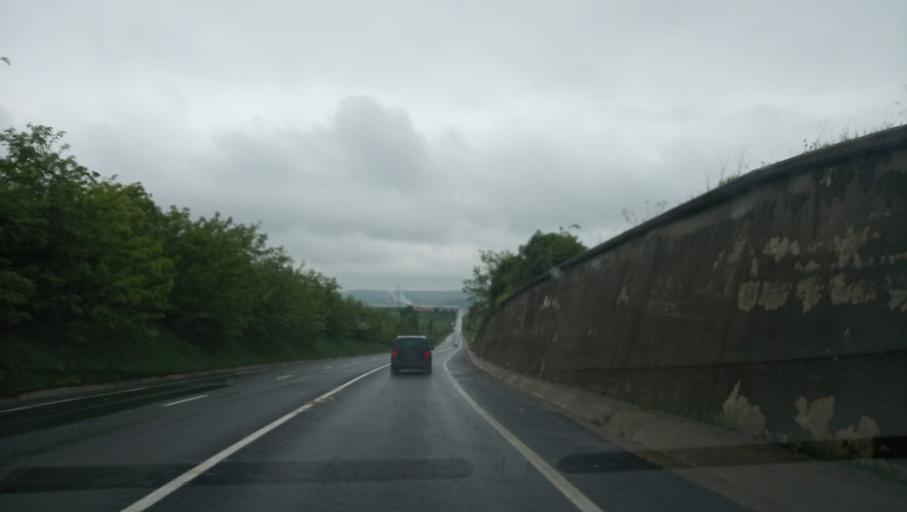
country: RO
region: Sibiu
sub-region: Oras Miercurea Sibiului
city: Miercurea Sibiului
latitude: 45.8692
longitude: 23.8058
